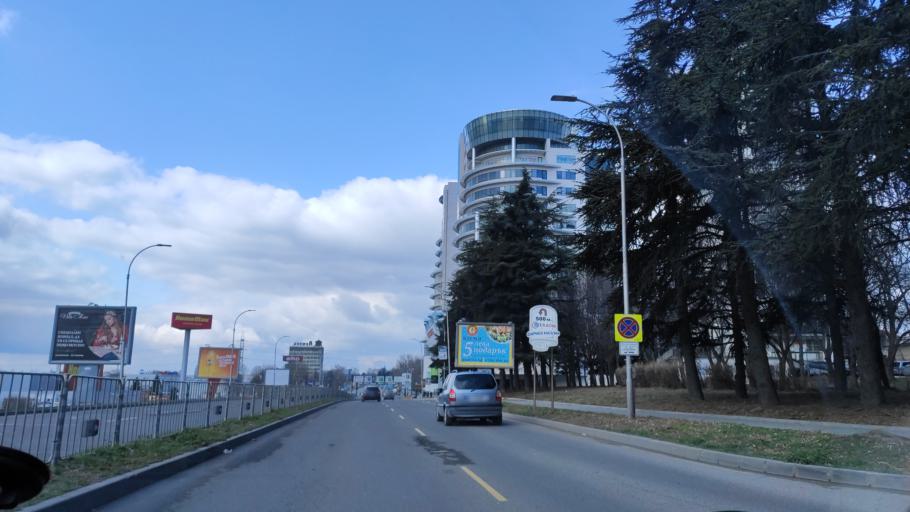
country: BG
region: Varna
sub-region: Obshtina Varna
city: Varna
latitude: 43.2212
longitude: 27.8787
